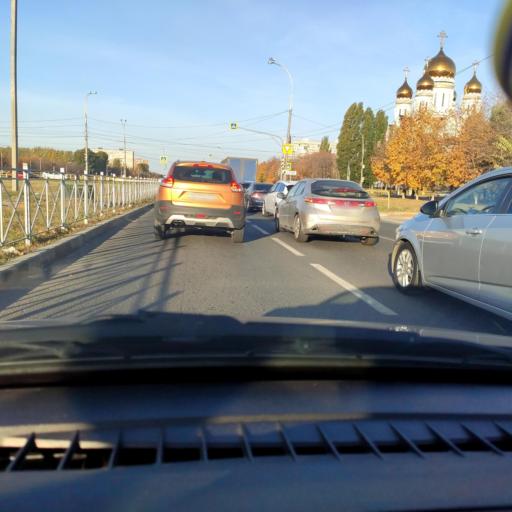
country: RU
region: Samara
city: Tol'yatti
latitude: 53.5199
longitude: 49.2809
